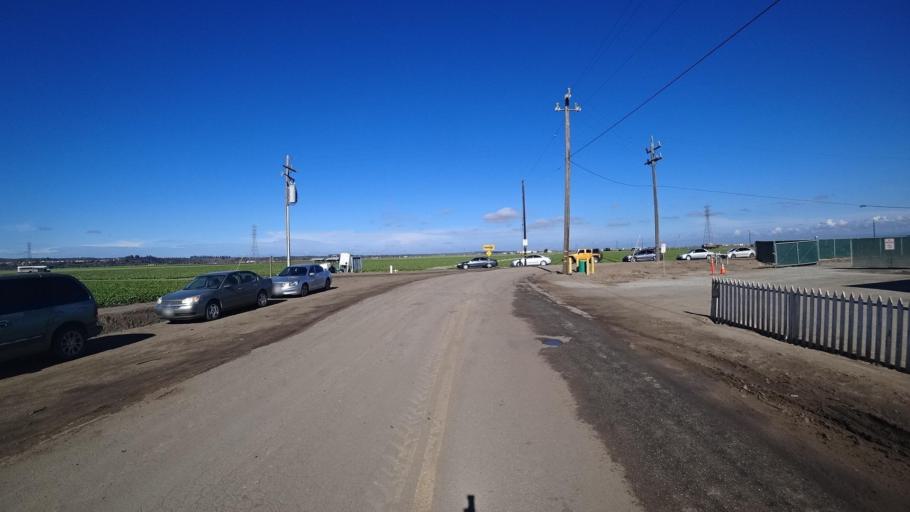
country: US
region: California
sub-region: Monterey County
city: Boronda
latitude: 36.6639
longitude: -121.7034
